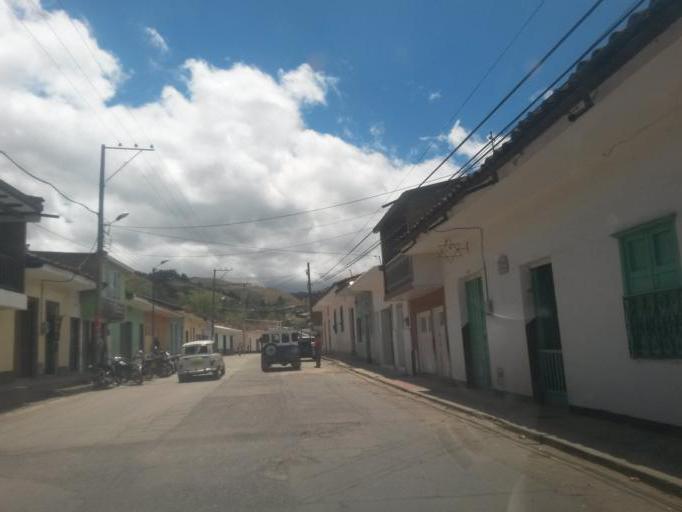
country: CO
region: Cauca
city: Silvia
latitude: 2.6140
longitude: -76.3755
